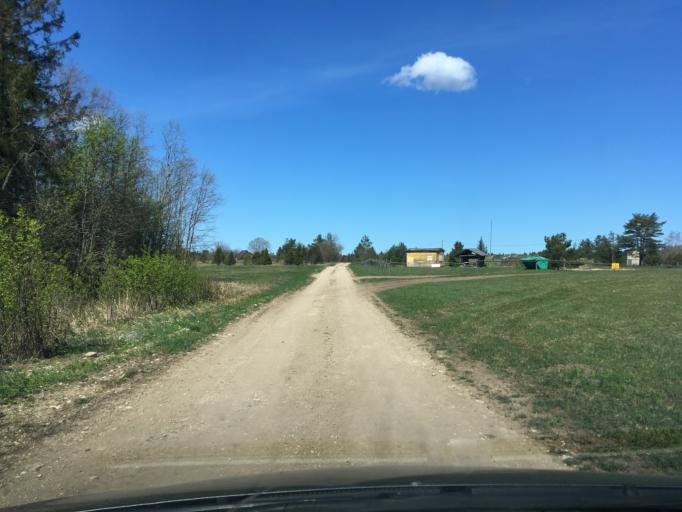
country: EE
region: Harju
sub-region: Raasiku vald
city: Raasiku
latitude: 59.2204
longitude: 25.1537
